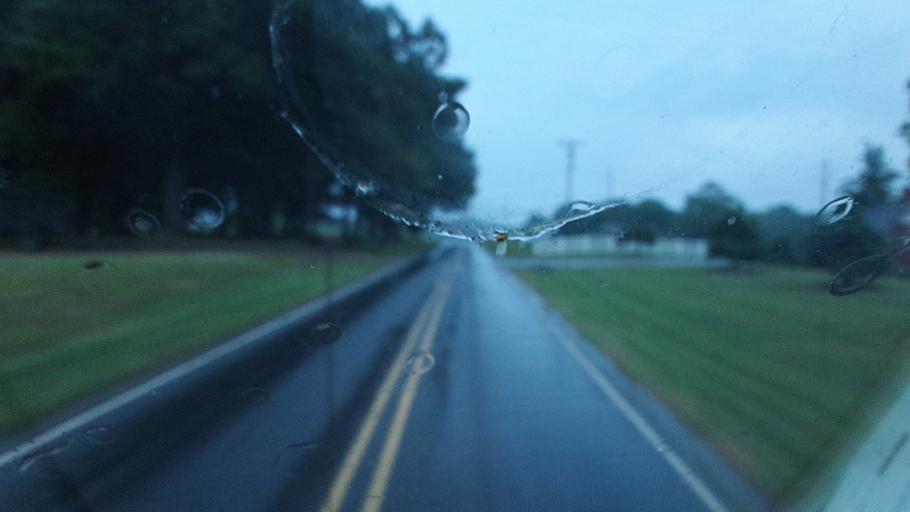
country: US
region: North Carolina
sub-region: Yadkin County
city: Jonesville
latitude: 36.0736
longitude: -80.8420
